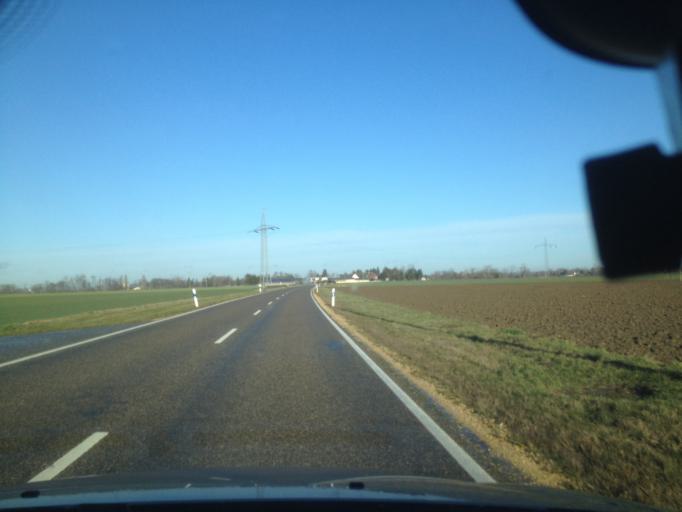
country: DE
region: Bavaria
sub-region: Swabia
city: Offingen
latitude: 48.4977
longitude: 10.3623
